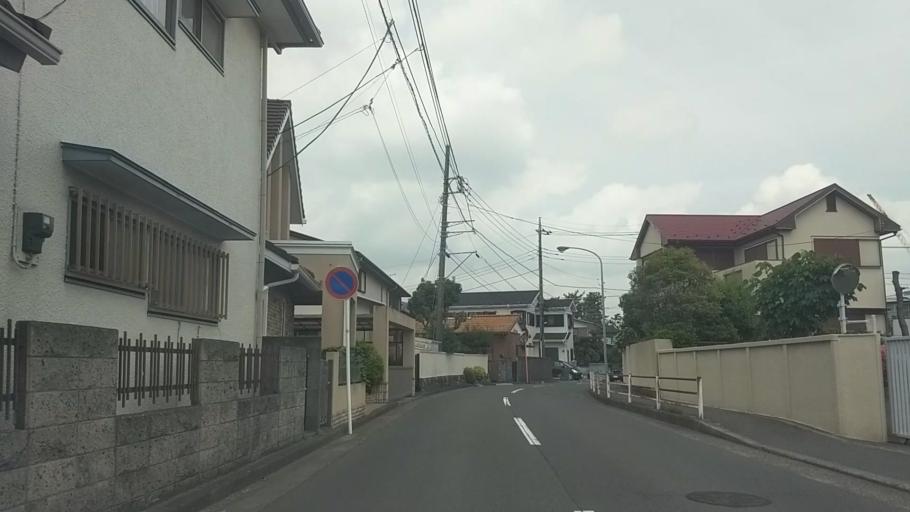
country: JP
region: Kanagawa
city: Fujisawa
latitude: 35.3597
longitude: 139.4737
